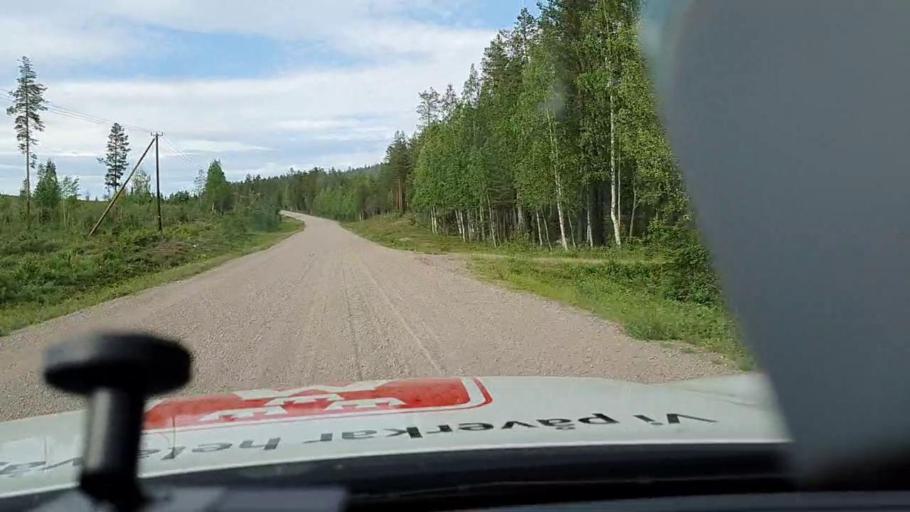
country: SE
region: Norrbotten
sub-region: Alvsbyns Kommun
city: AElvsbyn
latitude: 66.1274
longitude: 20.9973
